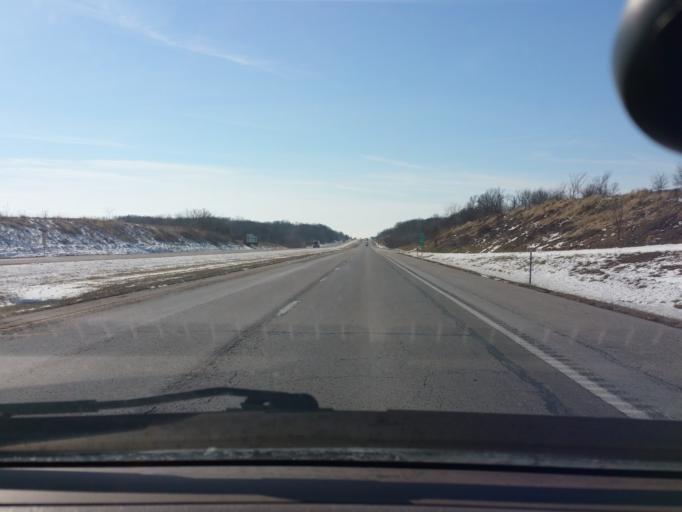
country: US
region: Missouri
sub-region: Harrison County
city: Bethany
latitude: 40.1038
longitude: -94.0726
